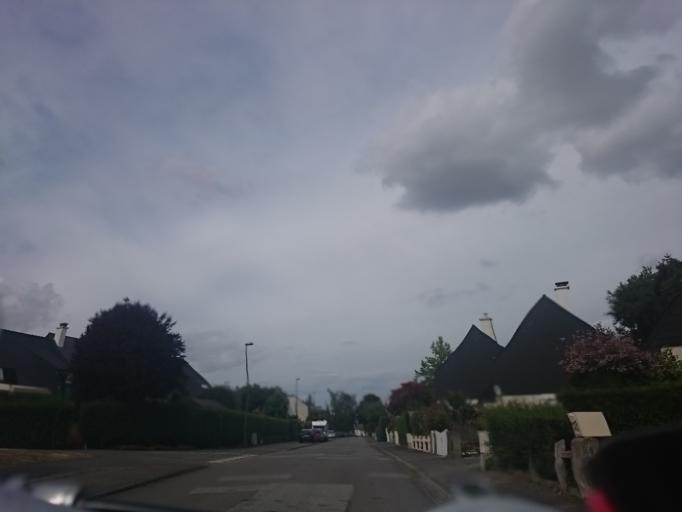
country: FR
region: Brittany
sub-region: Departement d'Ille-et-Vilaine
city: Cesson-Sevigne
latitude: 48.1204
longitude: -1.5958
